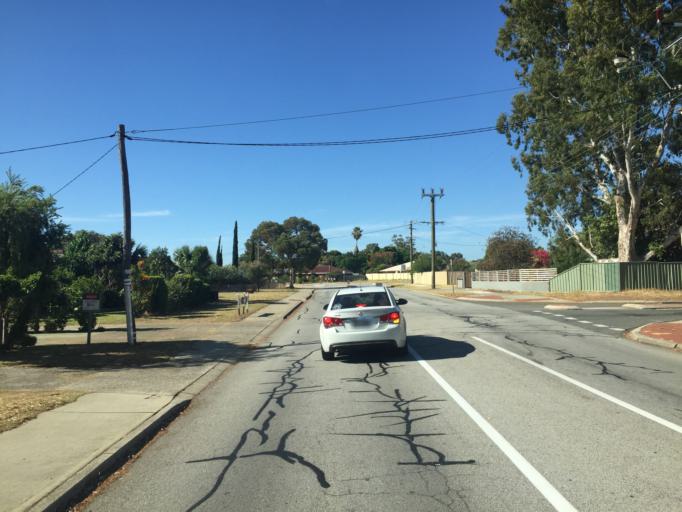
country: AU
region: Western Australia
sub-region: Gosnells
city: Maddington
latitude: -32.0523
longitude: 115.9999
